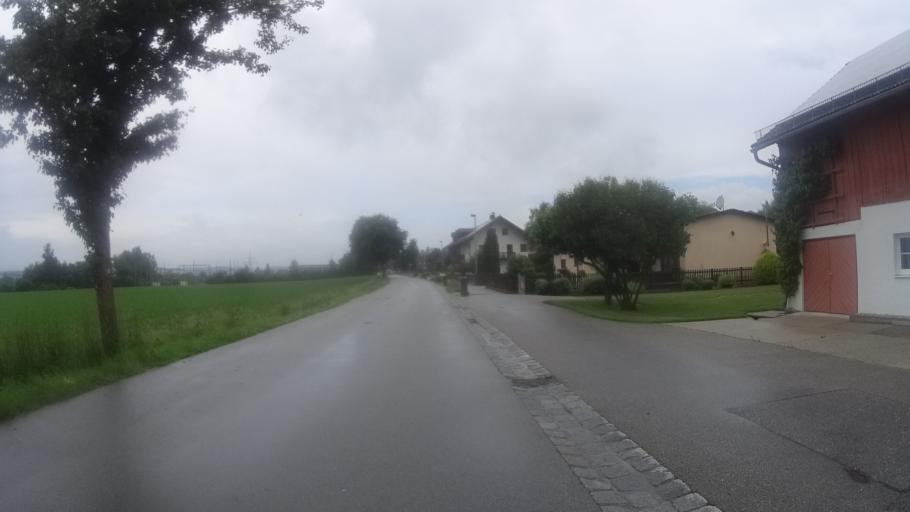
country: DE
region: Bavaria
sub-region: Lower Bavaria
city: Bad Griesbach
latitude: 48.4201
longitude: 13.1970
